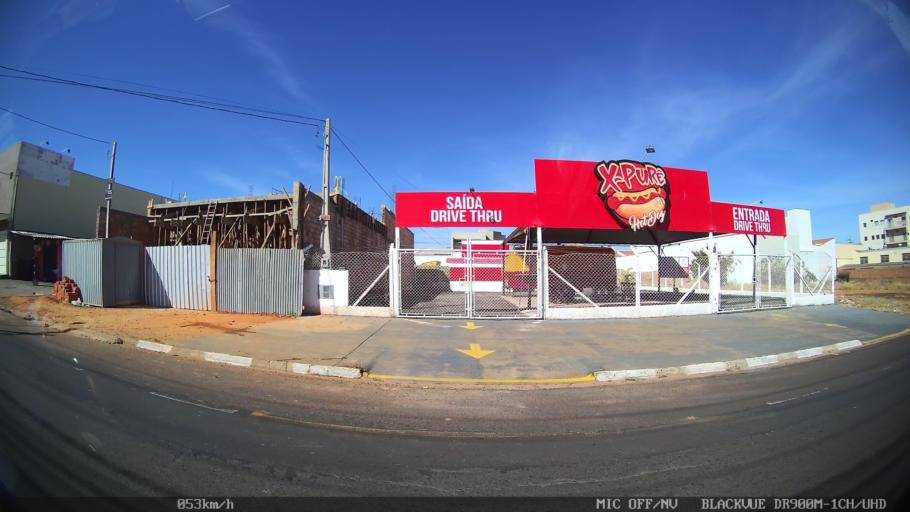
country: BR
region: Sao Paulo
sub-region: Franca
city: Franca
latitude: -20.5417
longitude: -47.3735
